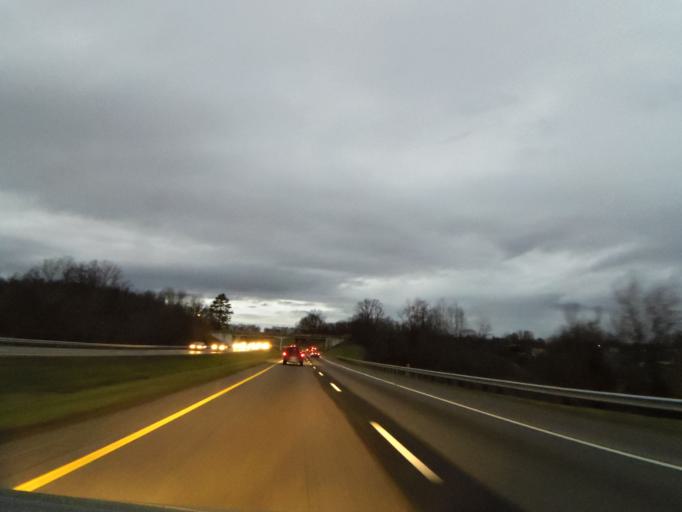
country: US
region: Tennessee
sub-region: Washington County
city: Oak Grove
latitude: 36.3924
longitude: -82.4464
